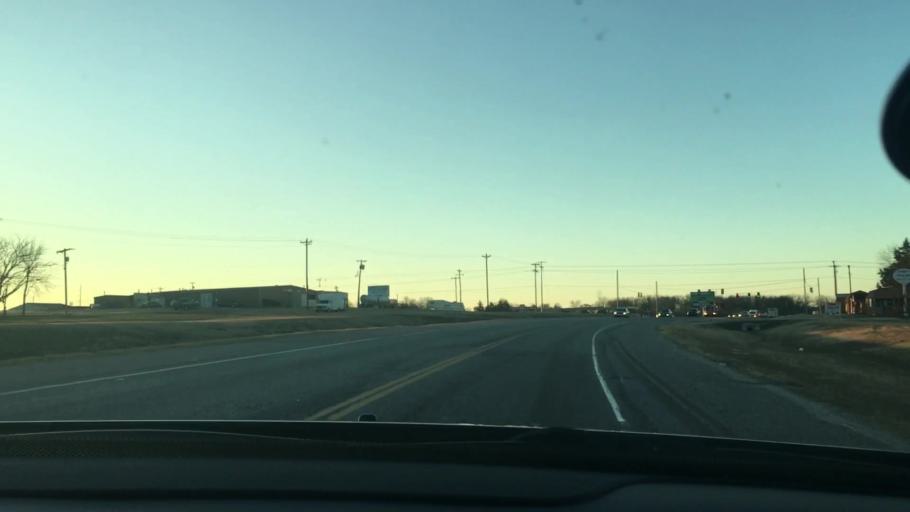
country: US
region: Oklahoma
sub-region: Pontotoc County
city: Ada
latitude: 34.7550
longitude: -96.7018
